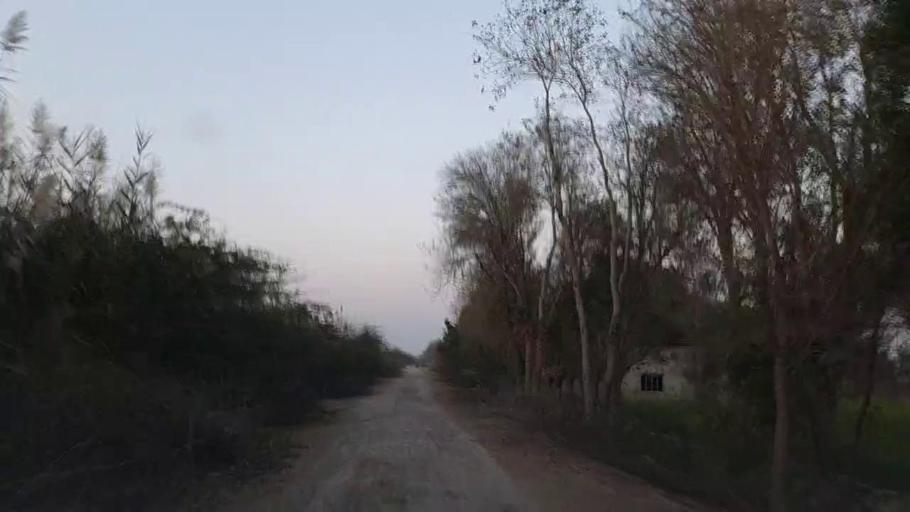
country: PK
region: Sindh
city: Bandhi
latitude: 26.6074
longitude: 68.3750
